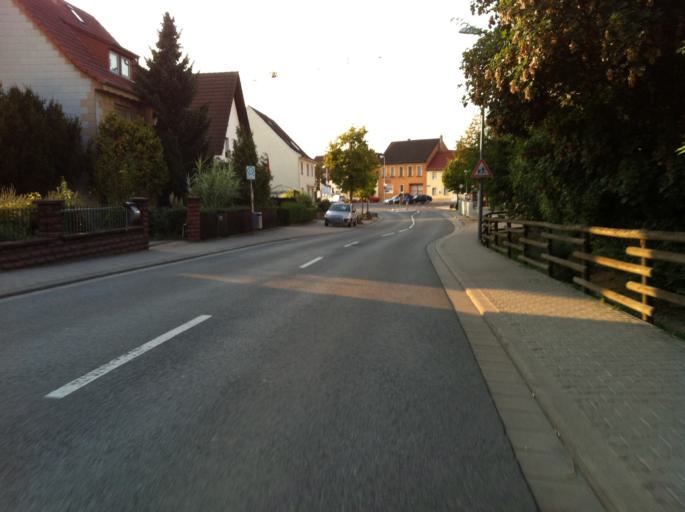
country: DE
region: Rheinland-Pfalz
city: Schwabenheim
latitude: 49.9430
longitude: 8.0808
